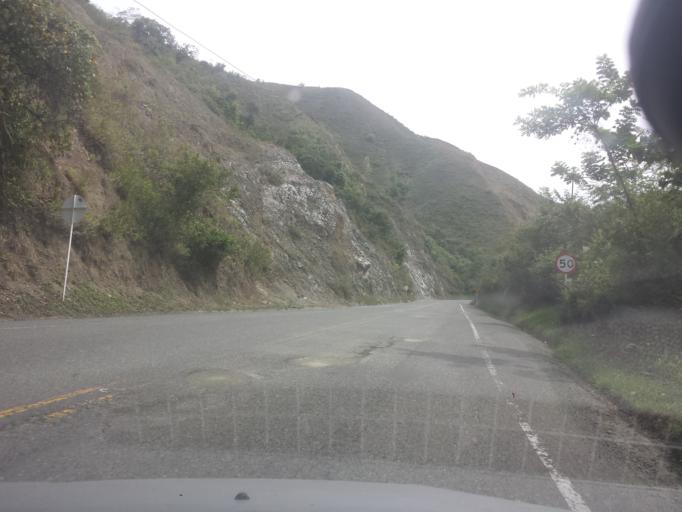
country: CO
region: Antioquia
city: Antioquia
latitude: 6.6204
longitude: -75.8746
